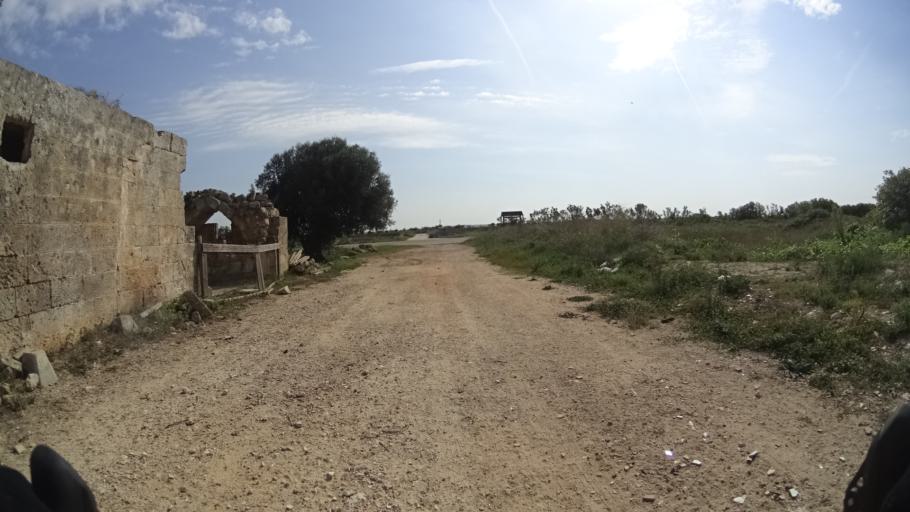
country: IT
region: Apulia
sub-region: Provincia di Taranto
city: Fragagnano
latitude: 40.4612
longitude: 17.4585
